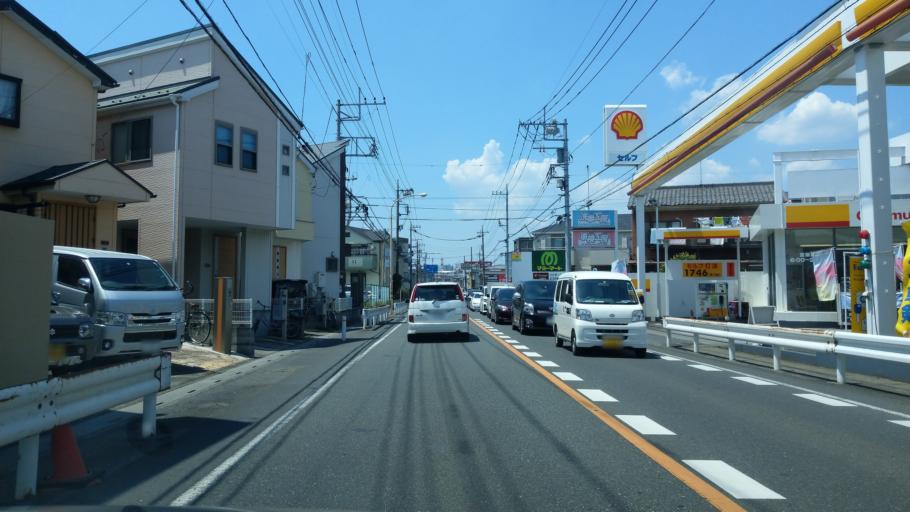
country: JP
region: Saitama
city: Yono
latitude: 35.8852
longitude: 139.6481
